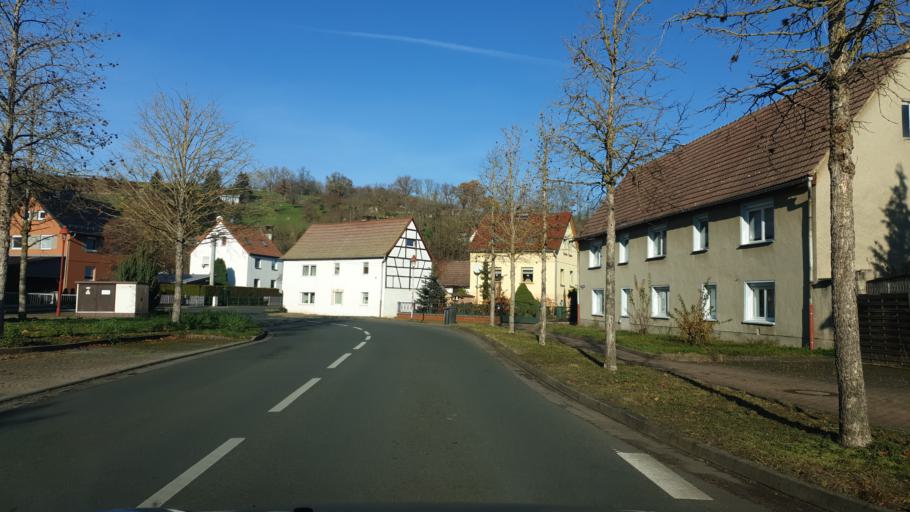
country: DE
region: Thuringia
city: Hartmannsdorf
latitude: 50.9778
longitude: 11.9790
